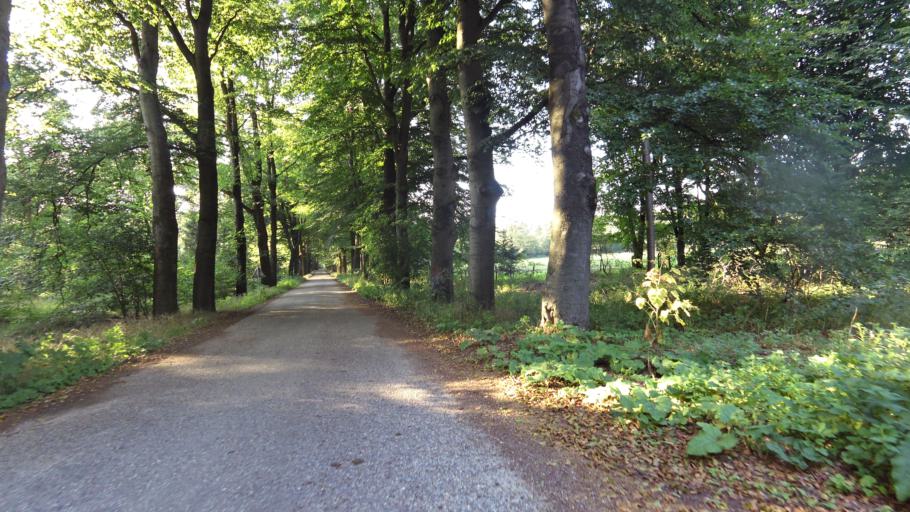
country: NL
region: Gelderland
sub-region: Gemeente Renkum
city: Oosterbeek
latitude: 52.0167
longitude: 5.8497
